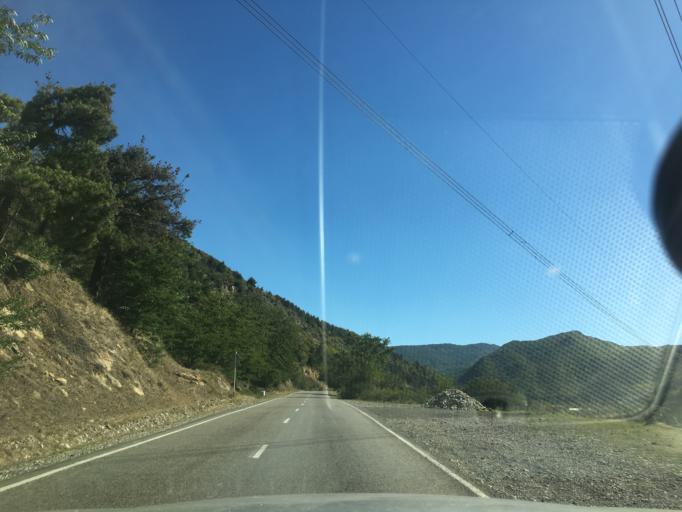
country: GE
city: Zahesi
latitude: 41.8276
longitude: 44.8304
